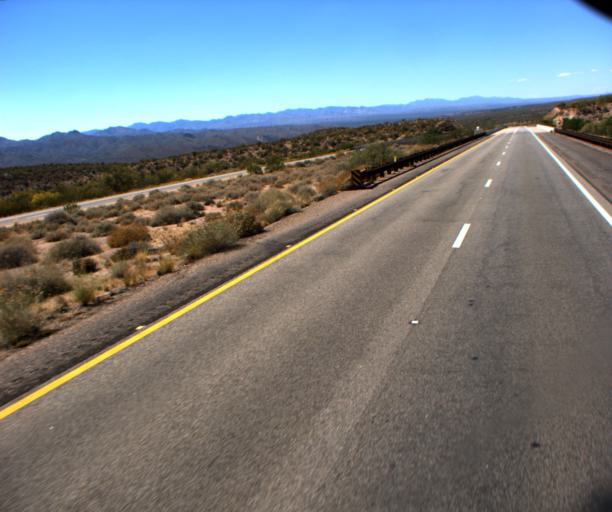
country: US
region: Arizona
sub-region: Yavapai County
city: Bagdad
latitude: 34.6124
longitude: -113.5257
